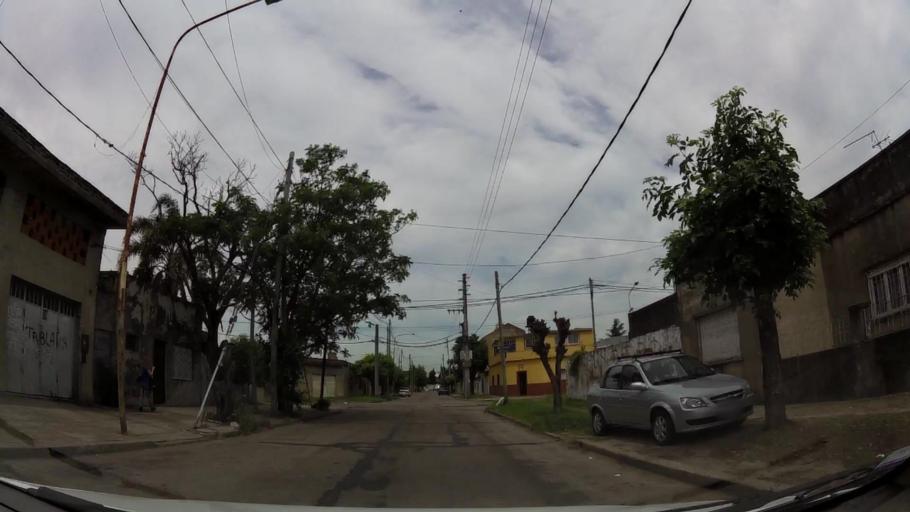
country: AR
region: Buenos Aires
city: San Justo
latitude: -34.6809
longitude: -58.5367
